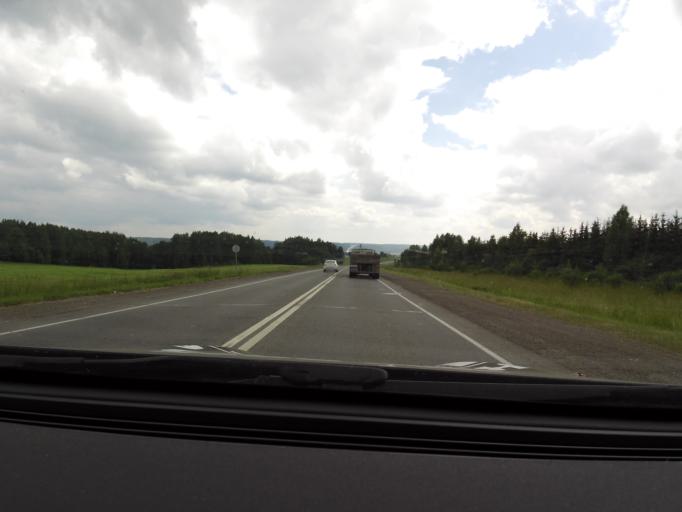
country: RU
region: Perm
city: Kungur
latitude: 57.3959
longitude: 56.8995
